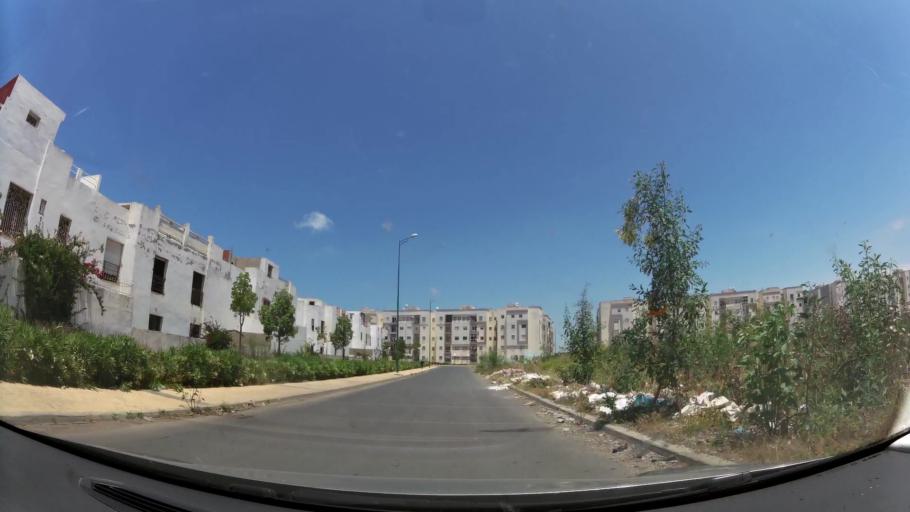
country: MA
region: Gharb-Chrarda-Beni Hssen
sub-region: Kenitra Province
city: Kenitra
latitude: 34.2528
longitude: -6.6469
